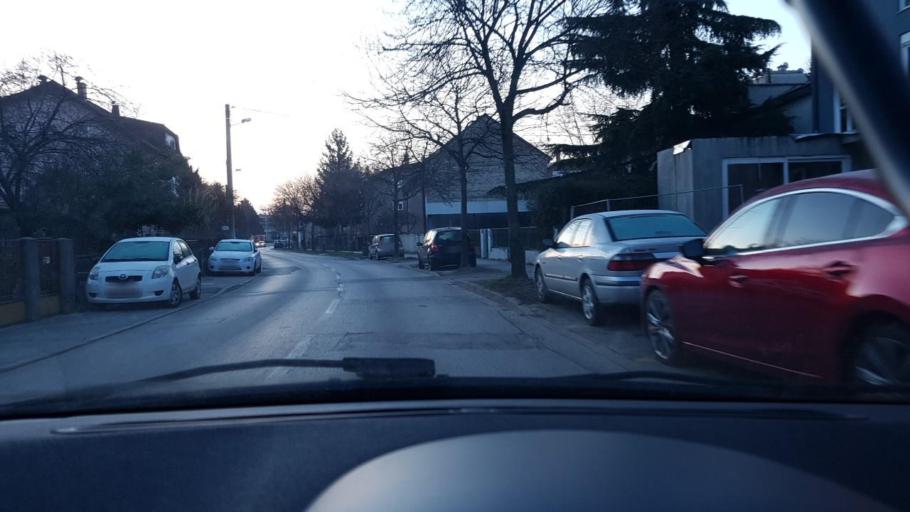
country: HR
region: Grad Zagreb
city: Zagreb
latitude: 45.8262
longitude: 16.0078
